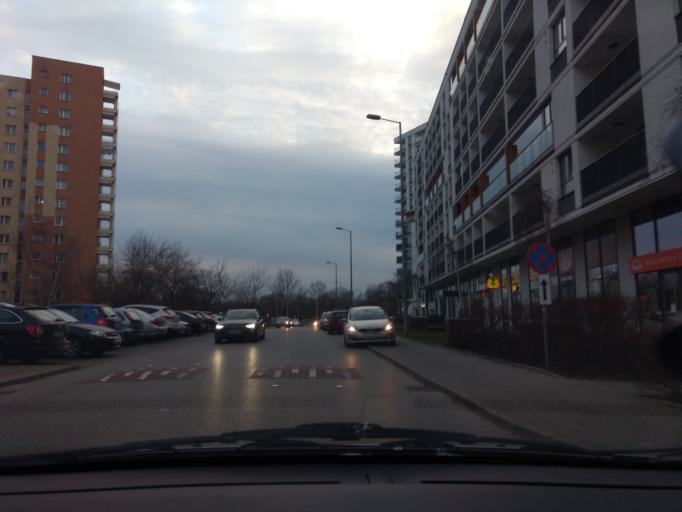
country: PL
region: Masovian Voivodeship
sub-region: Warszawa
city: Praga Poludnie
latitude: 52.2283
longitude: 21.0784
